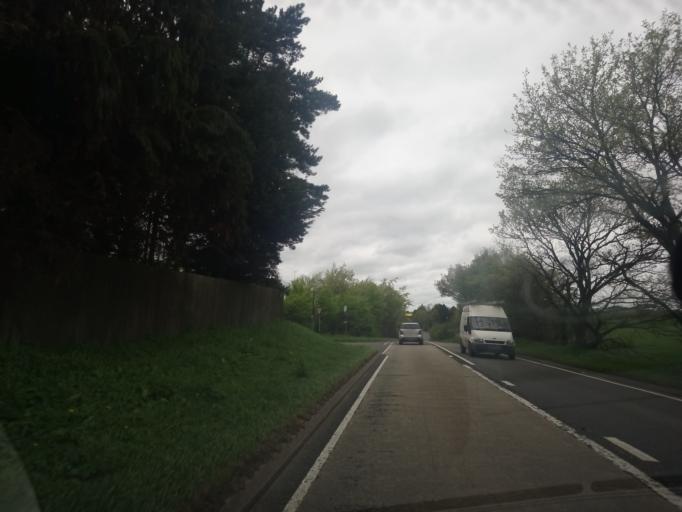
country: GB
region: England
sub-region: Telford and Wrekin
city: Chetwynd
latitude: 52.8074
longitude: -2.4362
